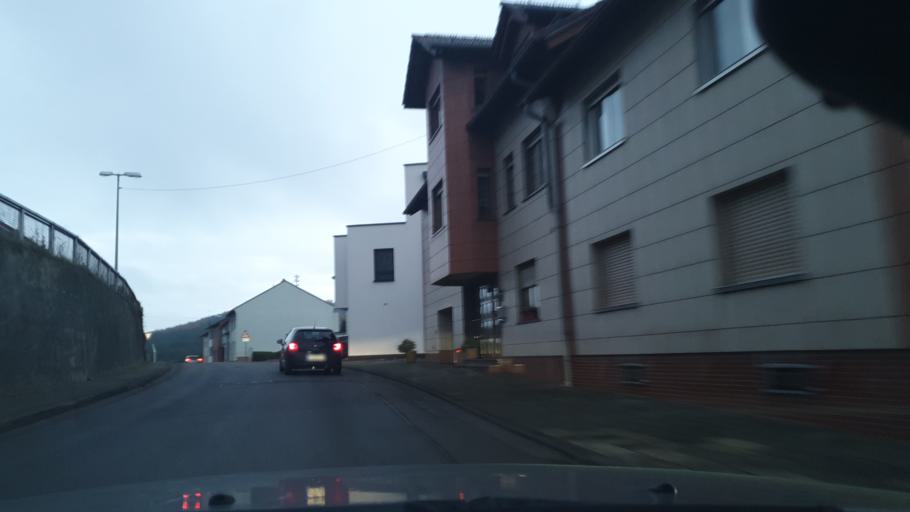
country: DE
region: Rheinland-Pfalz
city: Queidersbach
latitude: 49.3753
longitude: 7.6340
